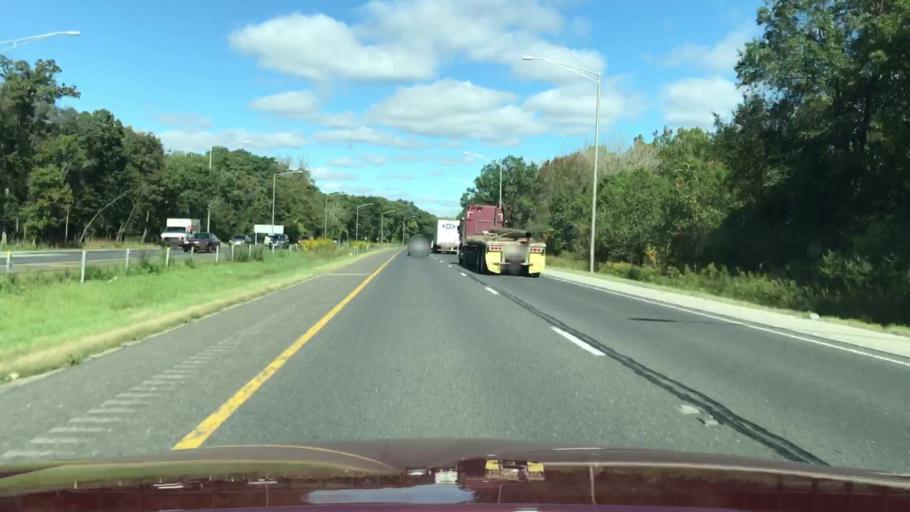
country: US
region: Illinois
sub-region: Cook County
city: Glenwood
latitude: 41.5495
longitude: -87.5828
